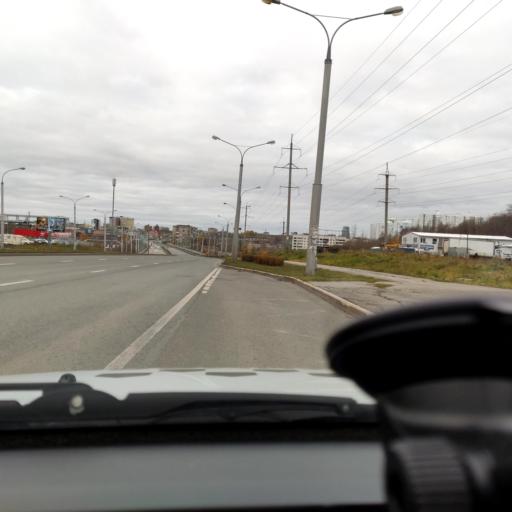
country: RU
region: Perm
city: Perm
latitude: 57.9888
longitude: 56.2871
